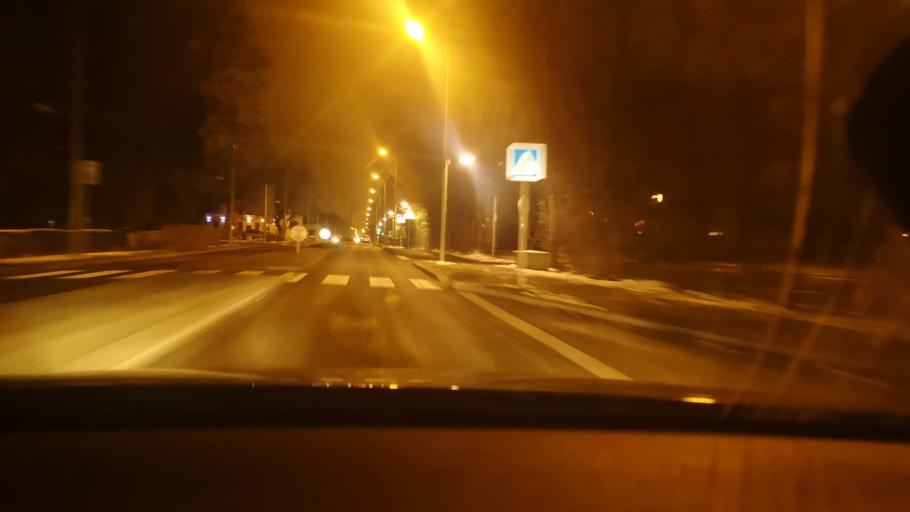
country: FR
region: Rhone-Alpes
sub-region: Departement de l'Ain
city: Montagnat
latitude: 46.1918
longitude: 5.2809
